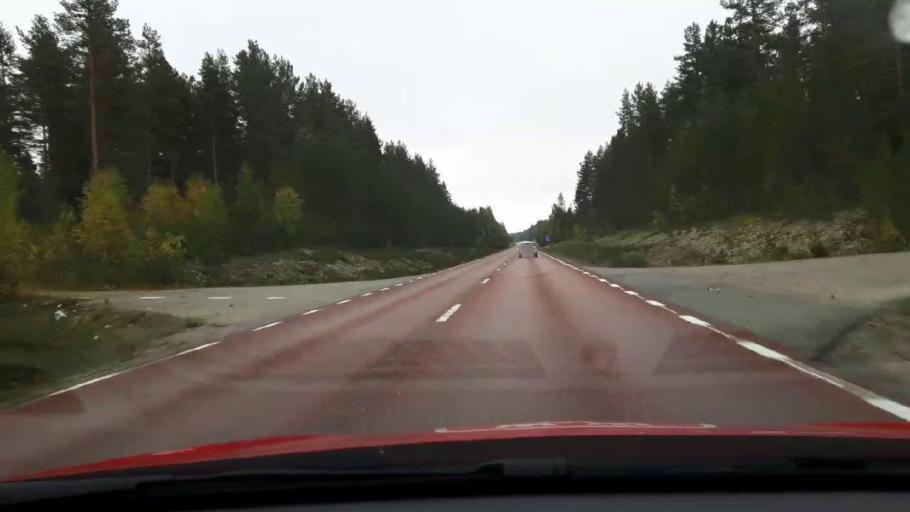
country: SE
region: Gaevleborg
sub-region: Ljusdals Kommun
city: Farila
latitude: 61.8128
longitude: 15.7673
